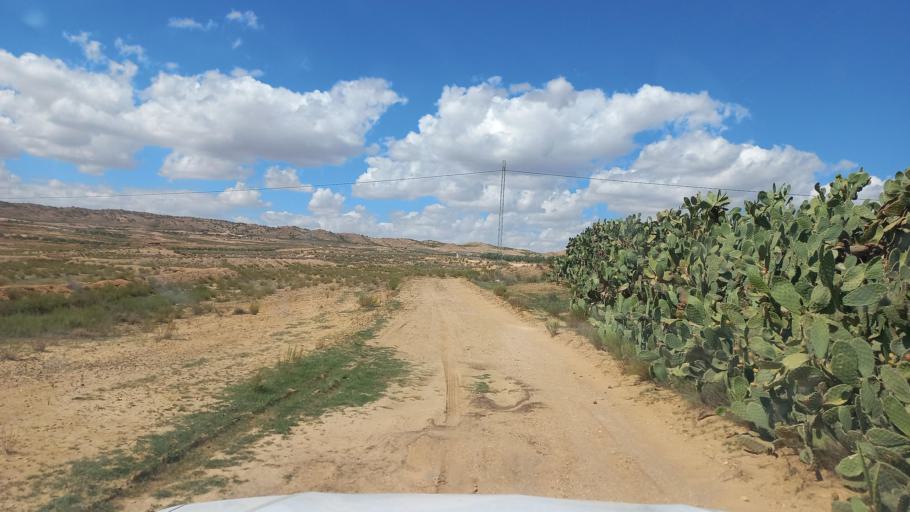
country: TN
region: Al Qasrayn
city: Sbiba
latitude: 35.3535
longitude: 9.0123
